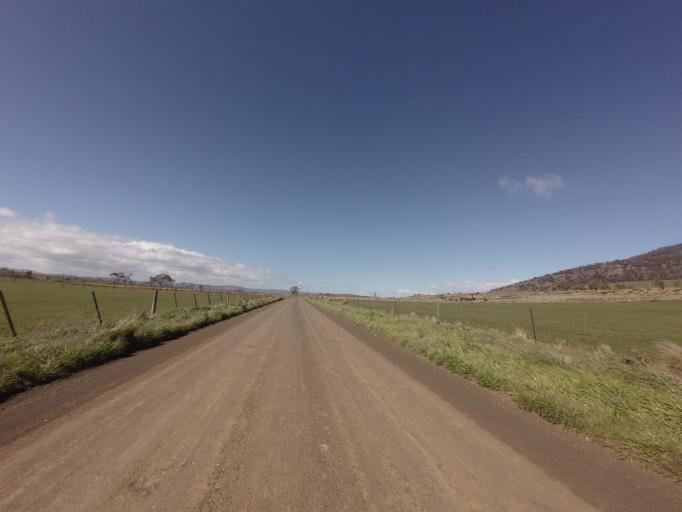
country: AU
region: Tasmania
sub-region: Northern Midlands
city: Evandale
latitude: -41.9218
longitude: 147.4018
